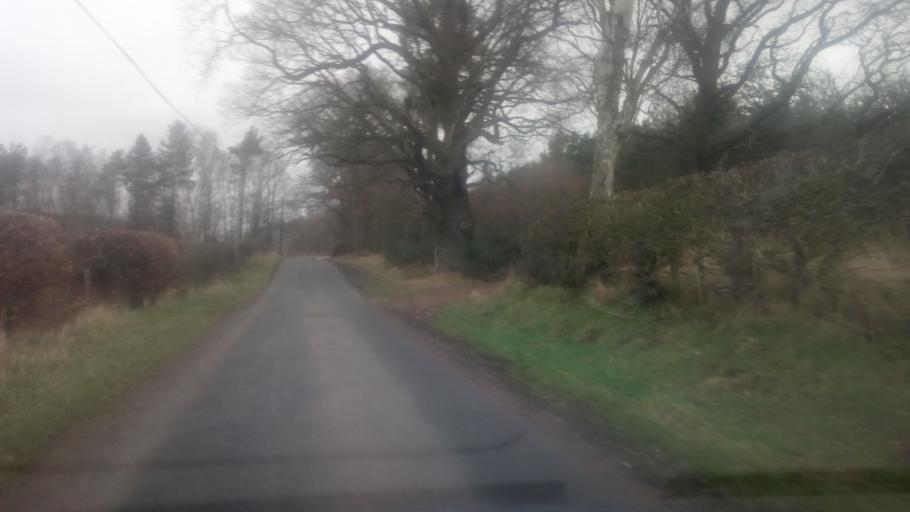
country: GB
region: Scotland
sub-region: The Scottish Borders
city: Jedburgh
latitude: 55.5326
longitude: -2.5034
